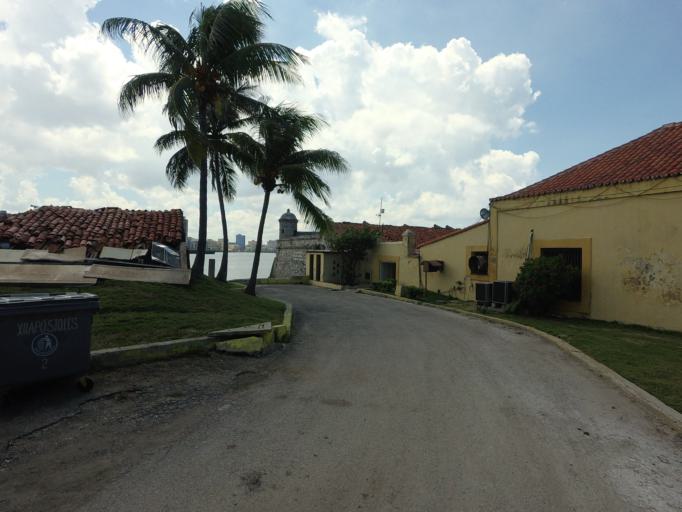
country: CU
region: La Habana
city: Centro Habana
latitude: 23.1497
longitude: -82.3558
